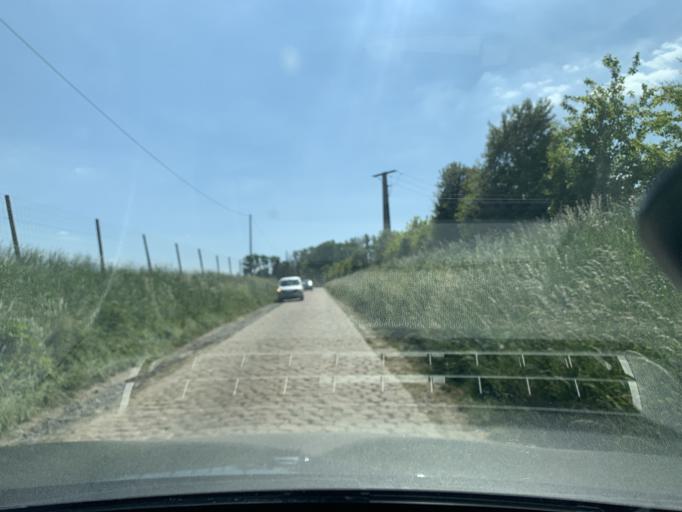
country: FR
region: Nord-Pas-de-Calais
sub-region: Departement du Nord
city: Caudry
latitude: 50.1034
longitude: 3.4196
